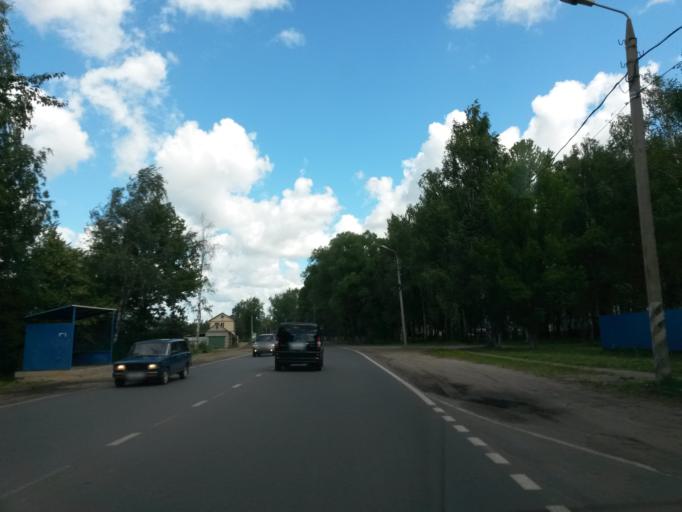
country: RU
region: Jaroslavl
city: Yaroslavl
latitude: 57.6547
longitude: 39.9083
